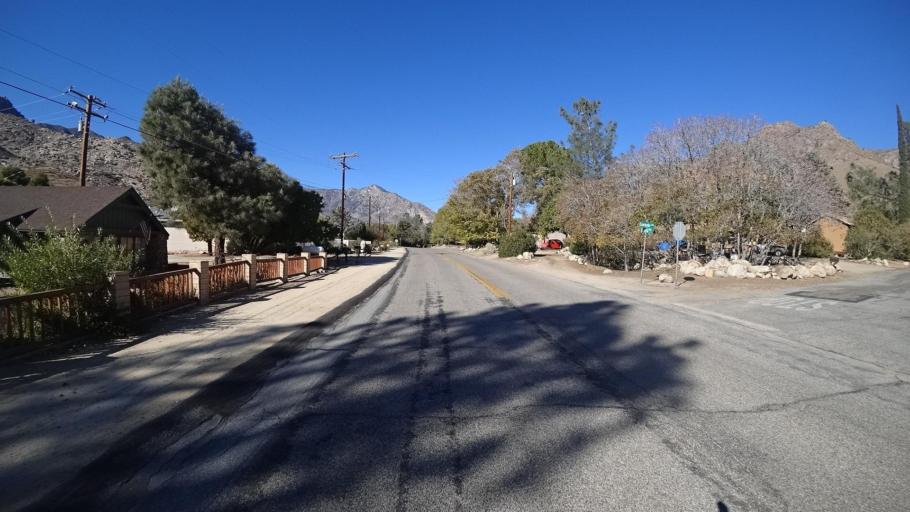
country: US
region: California
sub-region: Kern County
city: Kernville
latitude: 35.7877
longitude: -118.4469
